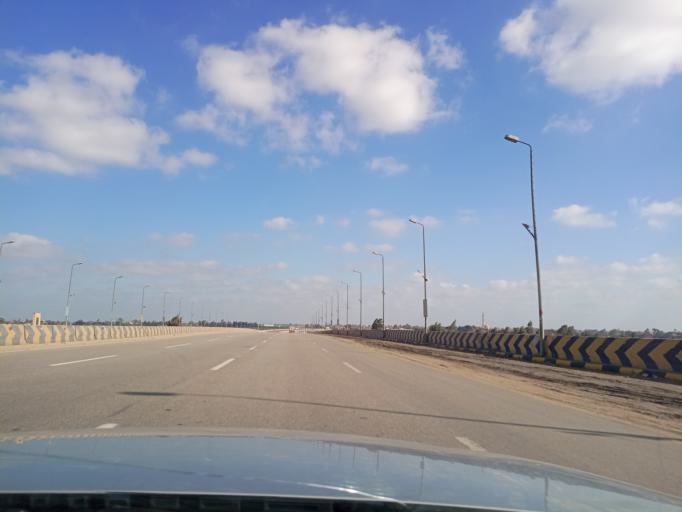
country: EG
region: Muhafazat al Minufiyah
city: Ashmun
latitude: 30.3259
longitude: 30.8329
